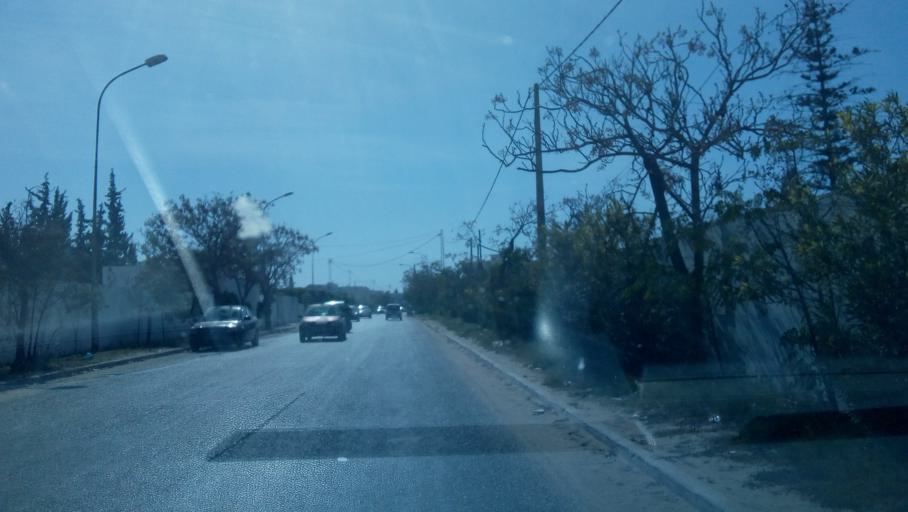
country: TN
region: Safaqis
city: Sfax
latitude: 34.7677
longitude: 10.7280
